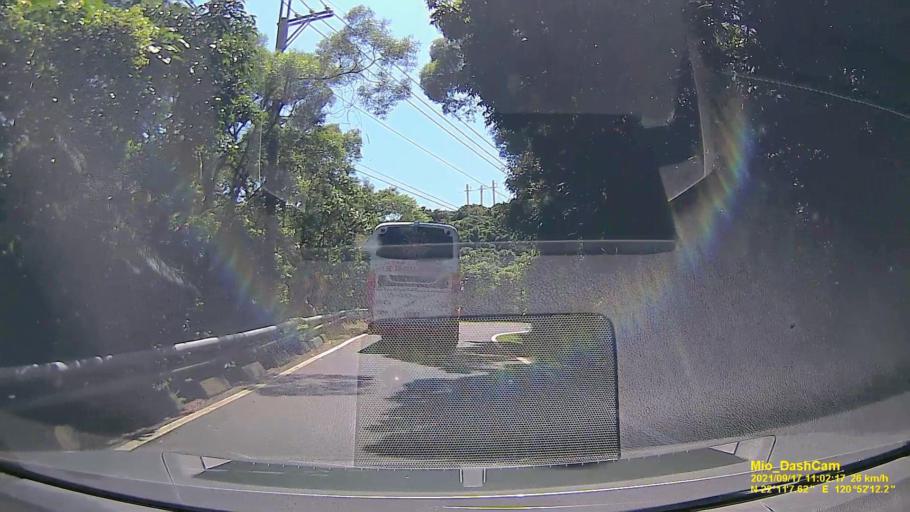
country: TW
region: Taiwan
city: Hengchun
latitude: 22.1854
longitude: 120.8701
